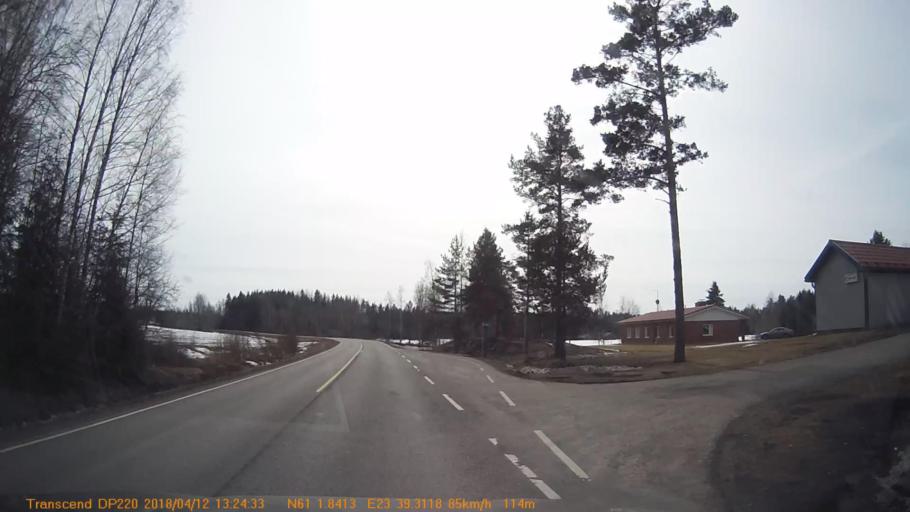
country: FI
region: Pirkanmaa
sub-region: Etelae-Pirkanmaa
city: Kylmaekoski
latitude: 61.0295
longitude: 23.6548
